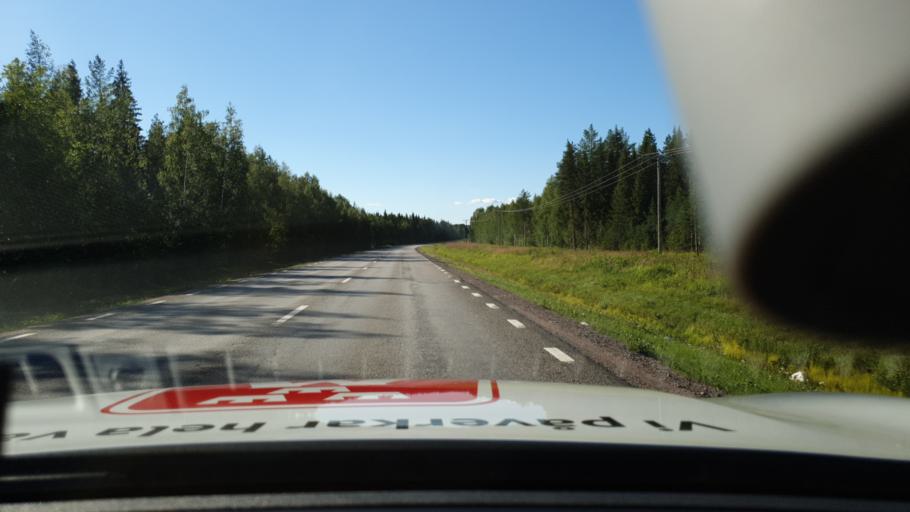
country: SE
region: Norrbotten
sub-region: Pitea Kommun
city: Rosvik
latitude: 65.5832
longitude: 21.6804
